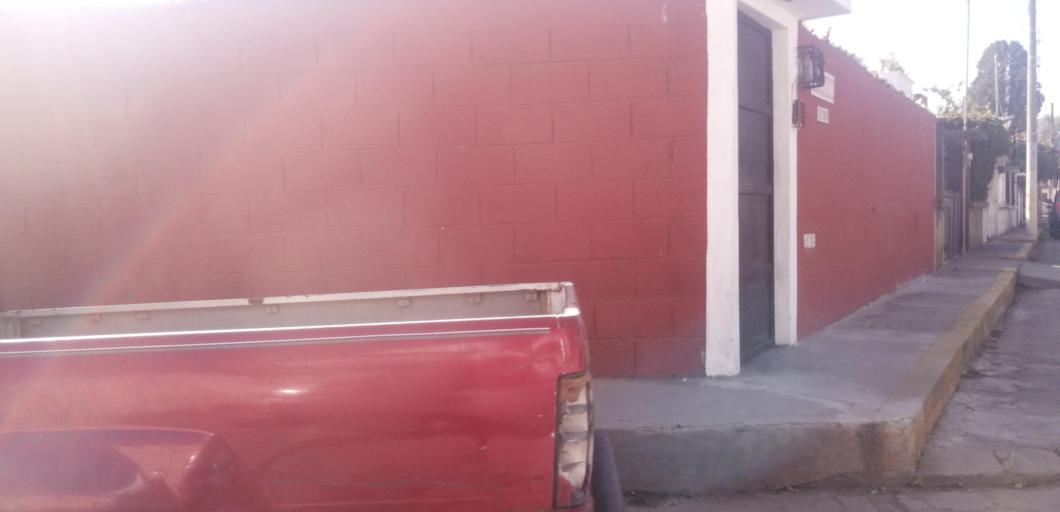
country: GT
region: Quetzaltenango
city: Quetzaltenango
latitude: 14.8410
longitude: -91.5326
